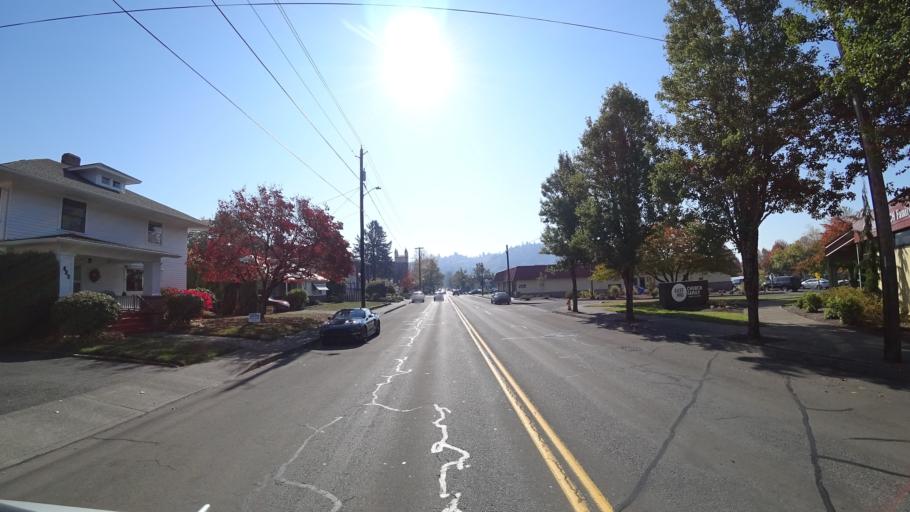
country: US
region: Oregon
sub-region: Multnomah County
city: Gresham
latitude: 45.5020
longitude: -122.4310
